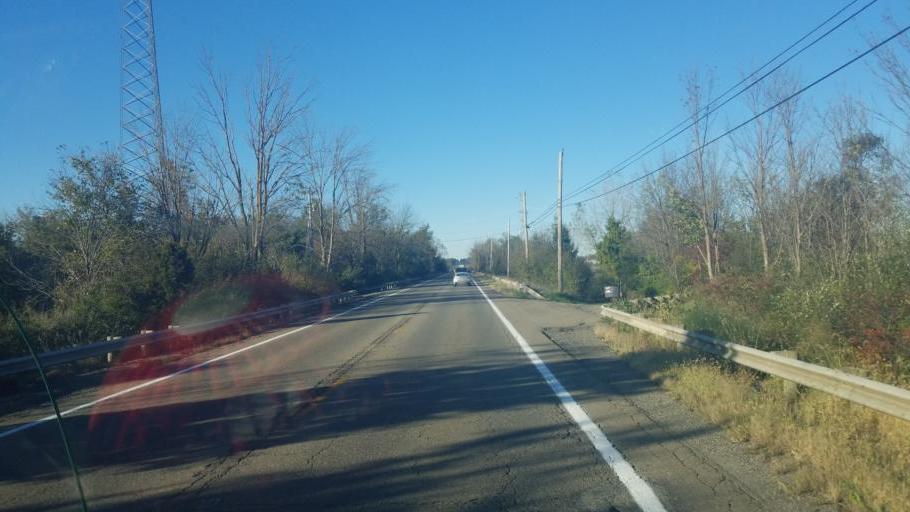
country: US
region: Ohio
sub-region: Columbiana County
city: Columbiana
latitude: 40.8744
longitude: -80.6508
